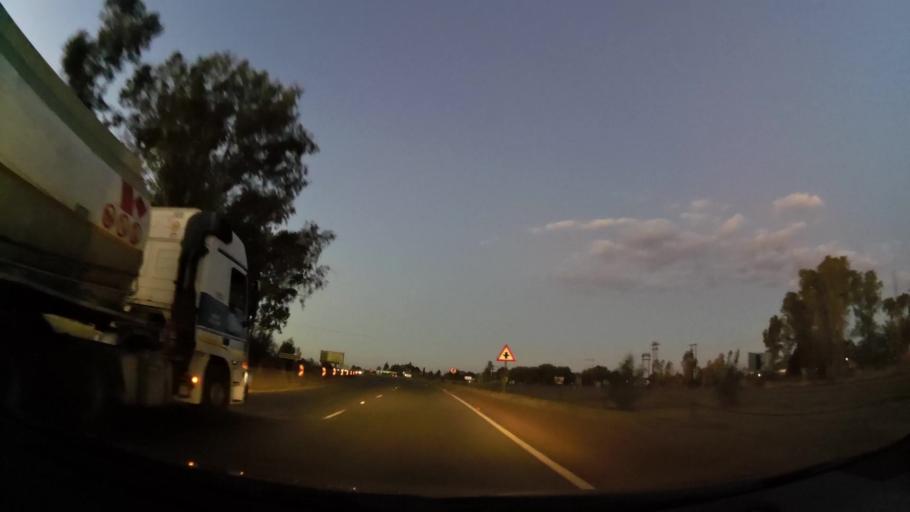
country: ZA
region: North-West
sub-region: Dr Kenneth Kaunda District Municipality
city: Potchefstroom
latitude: -26.7054
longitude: 27.1236
